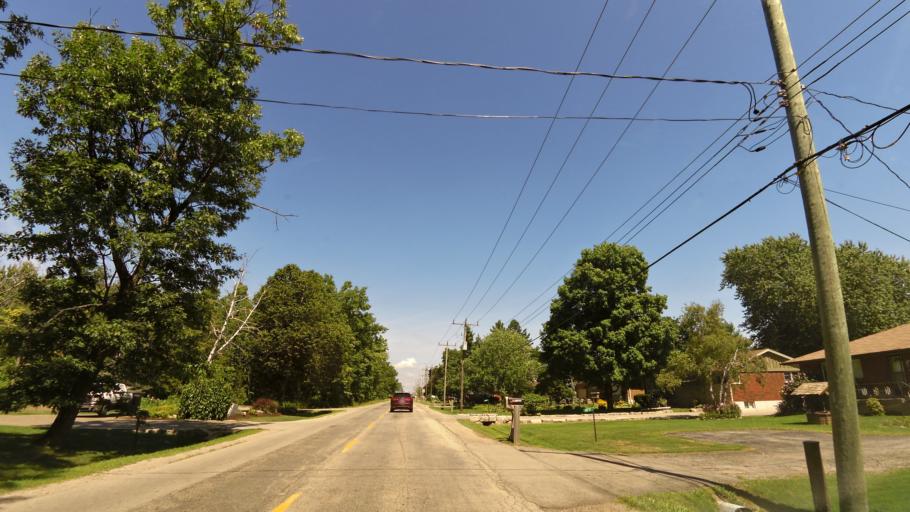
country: CA
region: Ontario
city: Ancaster
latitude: 43.1962
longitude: -79.9337
